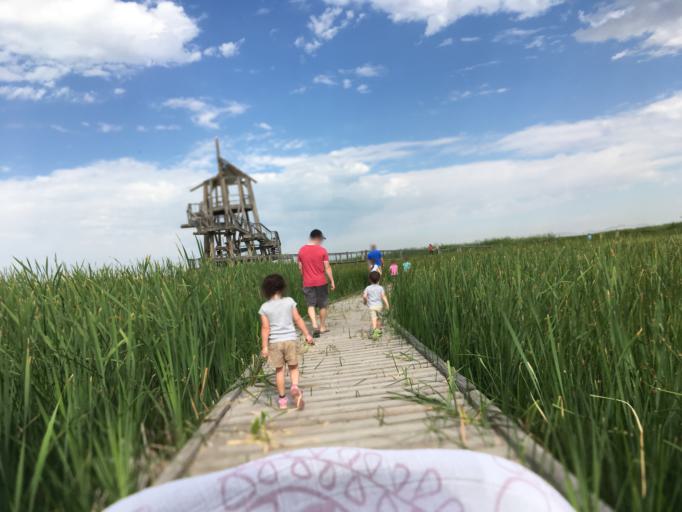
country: US
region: Utah
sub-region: Davis County
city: Layton
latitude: 41.0364
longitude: -112.0281
